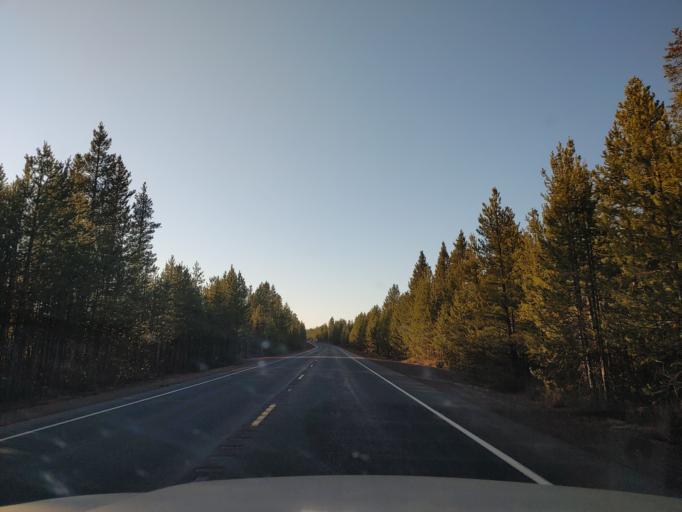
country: US
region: Oregon
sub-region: Deschutes County
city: La Pine
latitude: 43.4187
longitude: -121.8392
